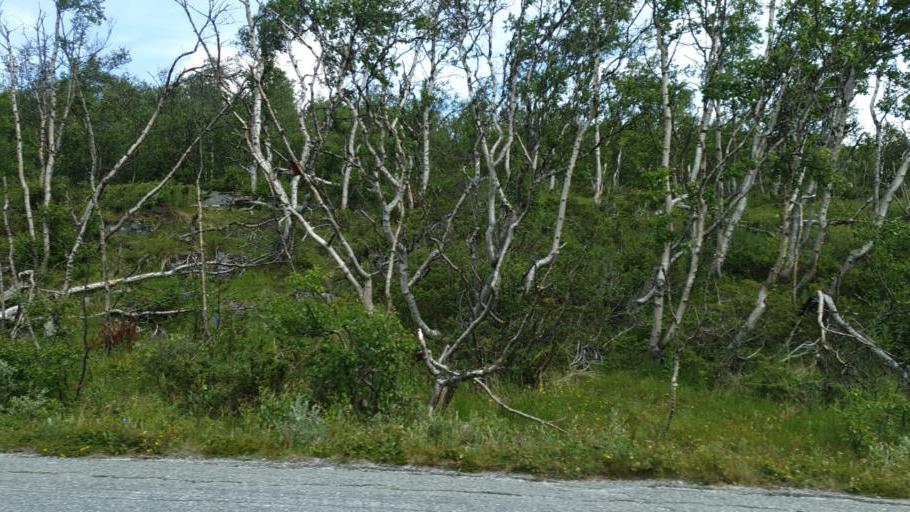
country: NO
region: Oppland
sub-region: Oystre Slidre
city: Heggenes
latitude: 61.4895
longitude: 8.8241
